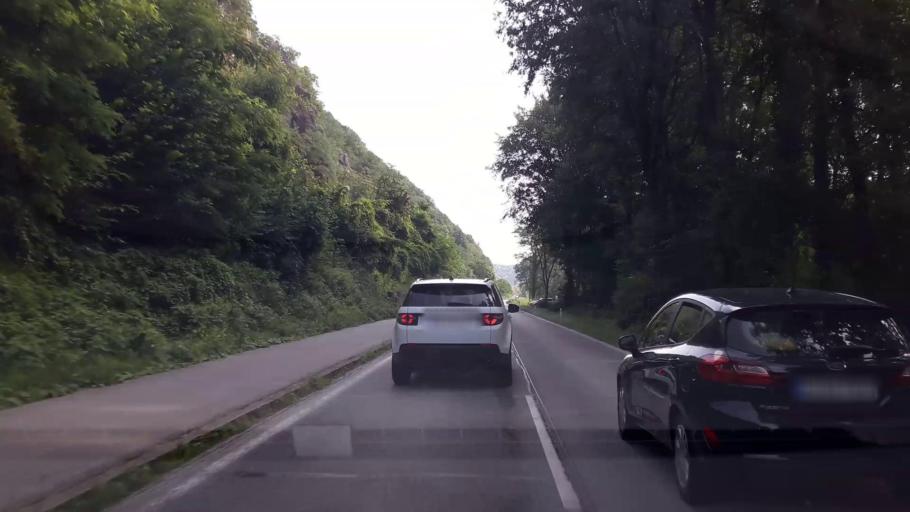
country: AT
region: Lower Austria
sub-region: Politischer Bezirk Krems
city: Aggsbach
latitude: 48.2749
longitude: 15.3824
